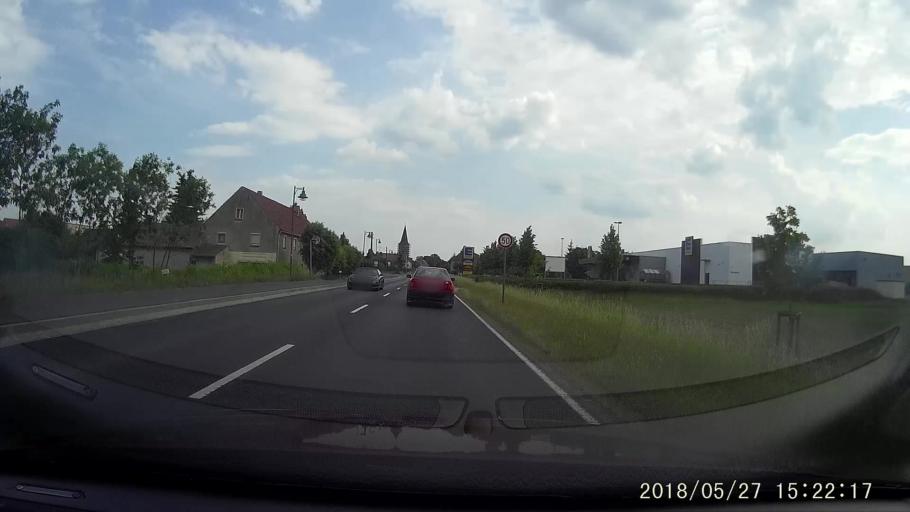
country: DE
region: Saxony
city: Kodersdorf
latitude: 51.2348
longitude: 14.8910
